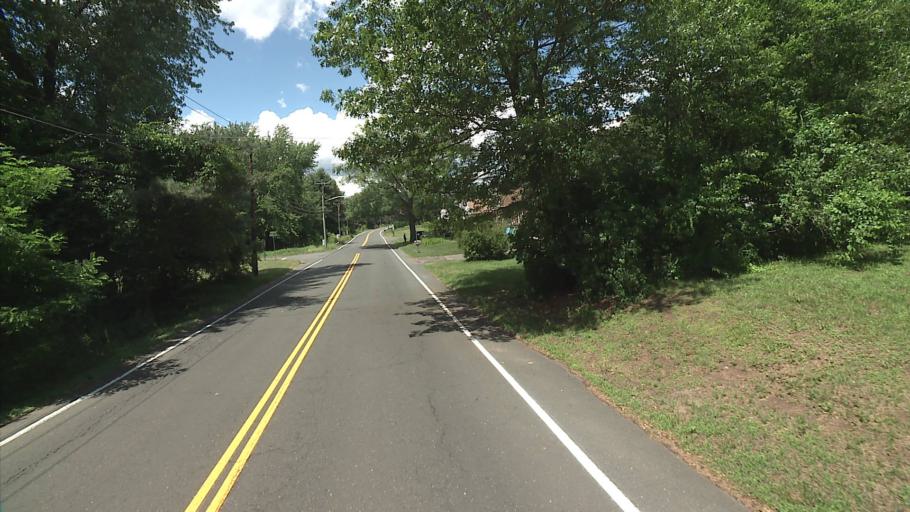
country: US
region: Connecticut
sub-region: Tolland County
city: Somers
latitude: 41.9959
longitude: -72.4869
